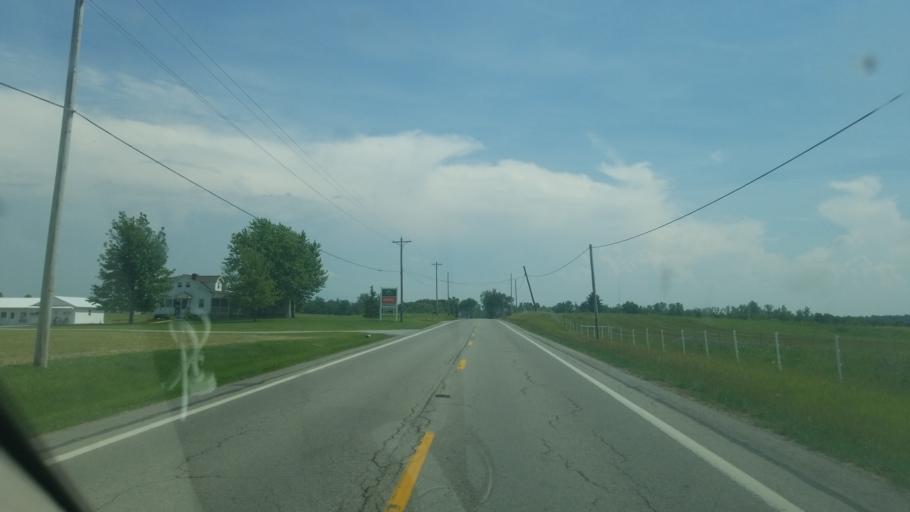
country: US
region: Ohio
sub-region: Logan County
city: Northwood
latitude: 40.4805
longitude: -83.7399
